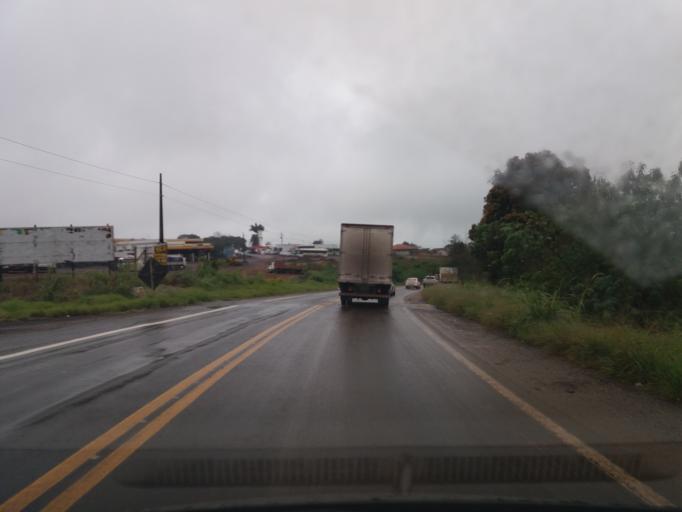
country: BR
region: Parana
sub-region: Realeza
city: Realeza
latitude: -25.4953
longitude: -53.5999
